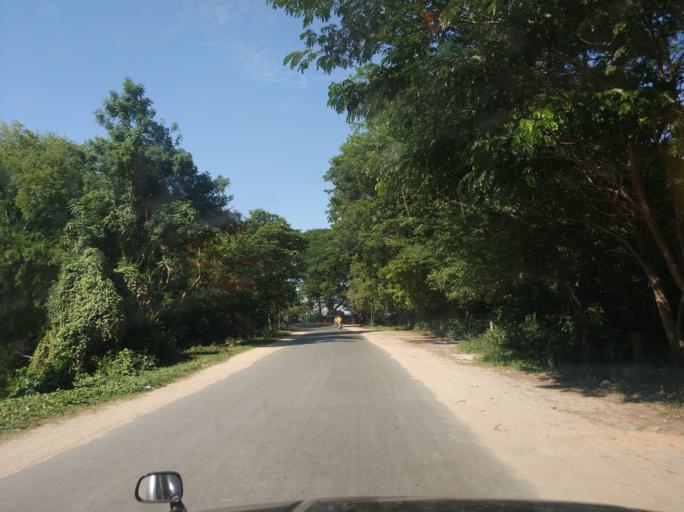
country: MM
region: Mandalay
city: Mandalay
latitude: 21.9545
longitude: 96.0514
